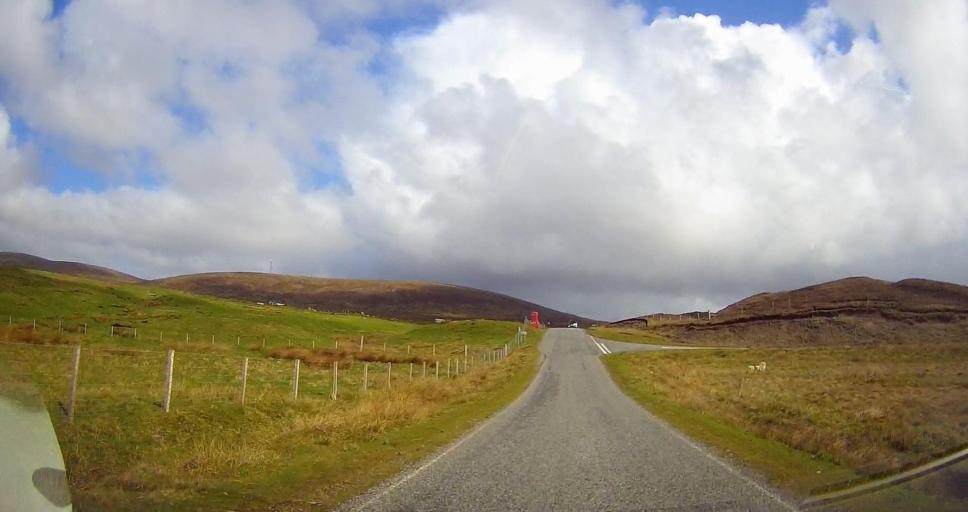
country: GB
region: Scotland
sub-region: Shetland Islands
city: Lerwick
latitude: 60.5181
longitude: -1.3774
